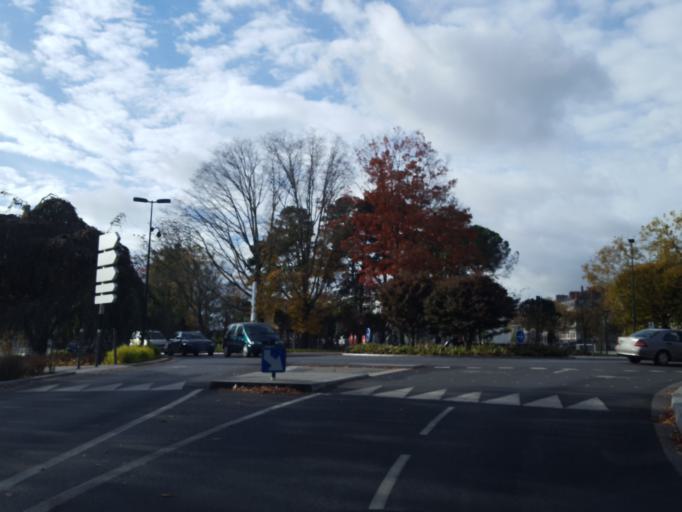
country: FR
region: Pays de la Loire
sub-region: Departement de la Loire-Atlantique
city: Nantes
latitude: 47.2145
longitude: -1.5497
